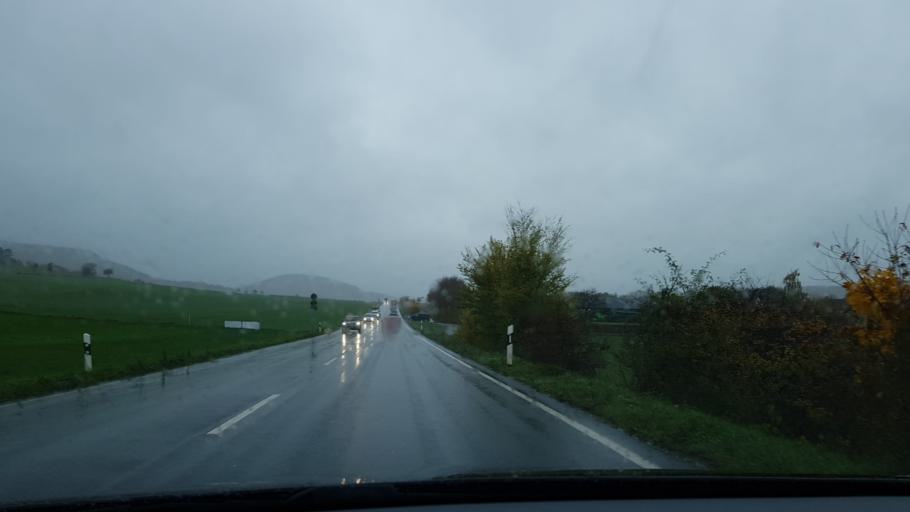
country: DE
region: Rheinland-Pfalz
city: Wittlich
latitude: 49.9688
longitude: 6.8610
